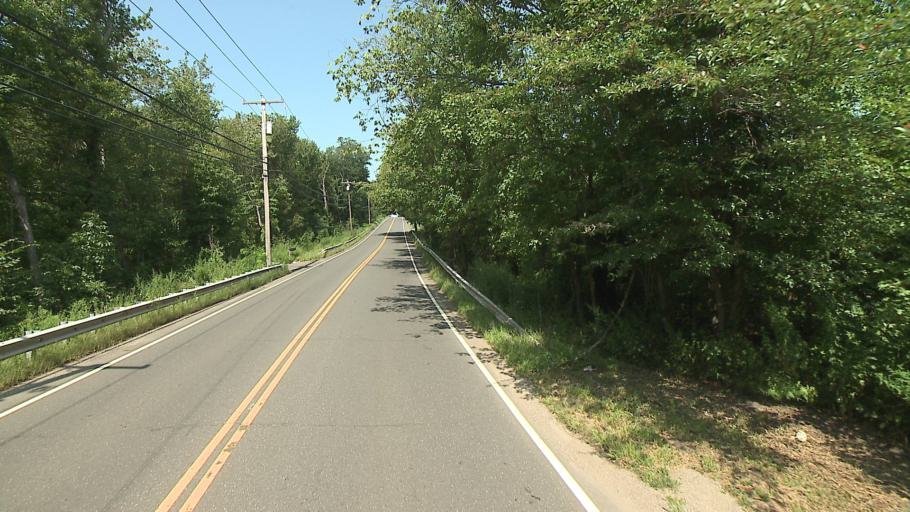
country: US
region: Connecticut
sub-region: Fairfield County
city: Trumbull
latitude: 41.2564
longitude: -73.2847
